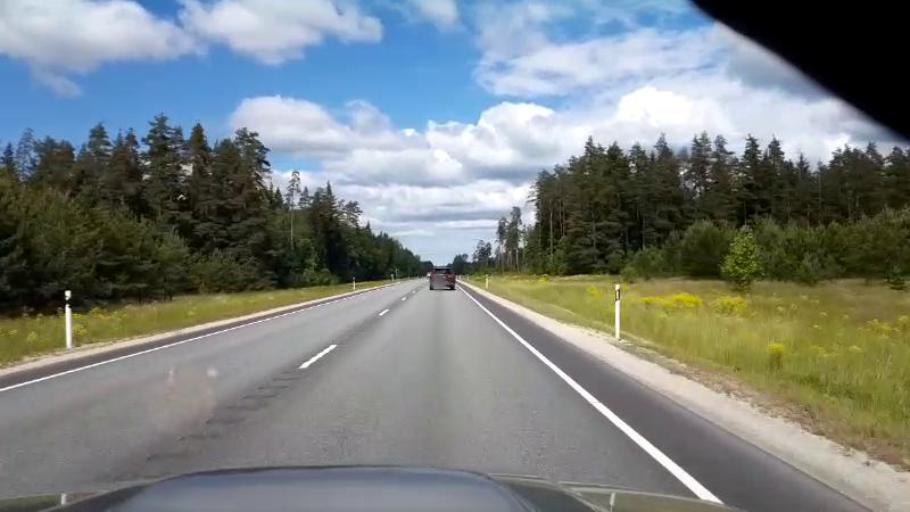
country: EE
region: Harju
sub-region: Nissi vald
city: Riisipere
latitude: 59.0922
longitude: 24.4645
